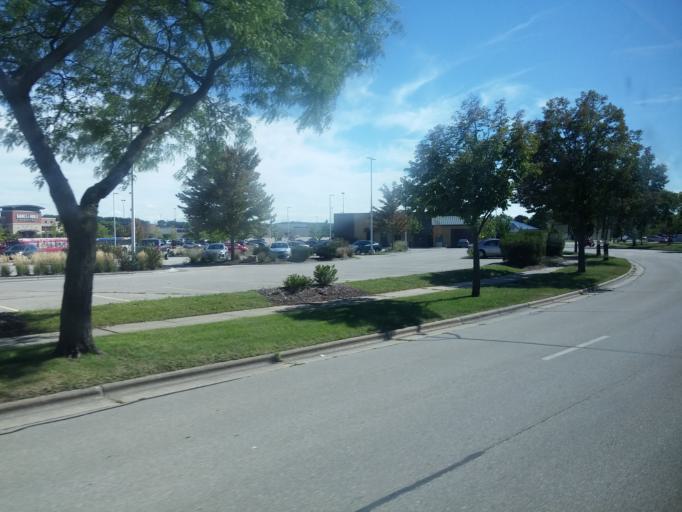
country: US
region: Wisconsin
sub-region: Dane County
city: Monona
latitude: 43.1272
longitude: -89.3077
